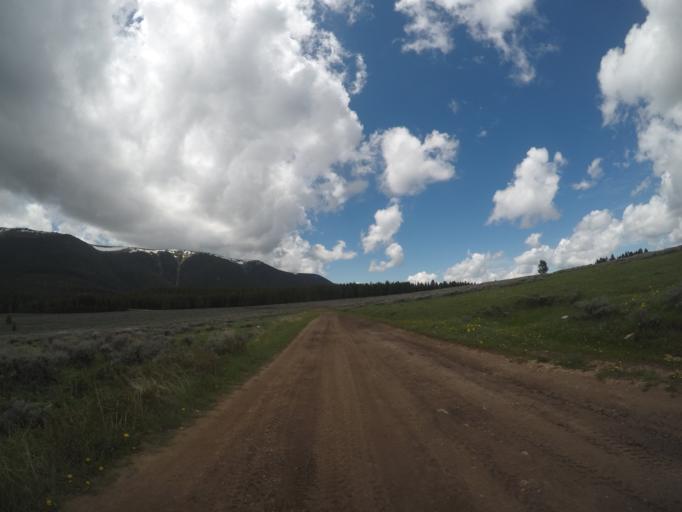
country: US
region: Wyoming
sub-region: Big Horn County
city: Lovell
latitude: 45.1791
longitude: -108.4448
